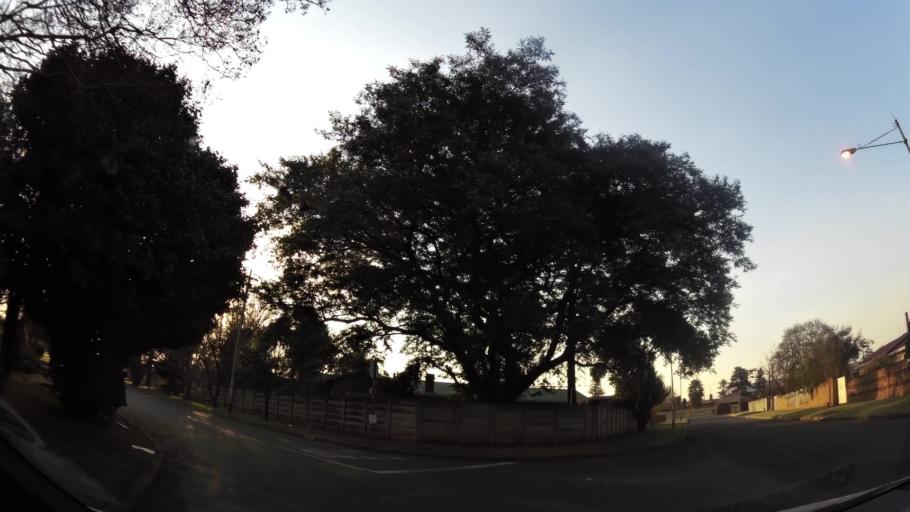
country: ZA
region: Gauteng
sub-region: Ekurhuleni Metropolitan Municipality
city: Springs
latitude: -26.2661
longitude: 28.4144
